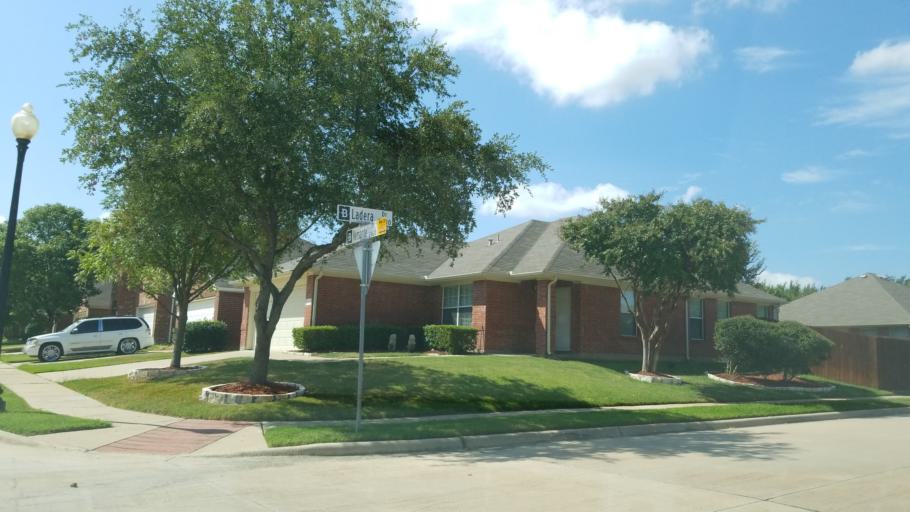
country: US
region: Texas
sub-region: Tarrant County
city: Euless
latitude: 32.8576
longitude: -97.1048
